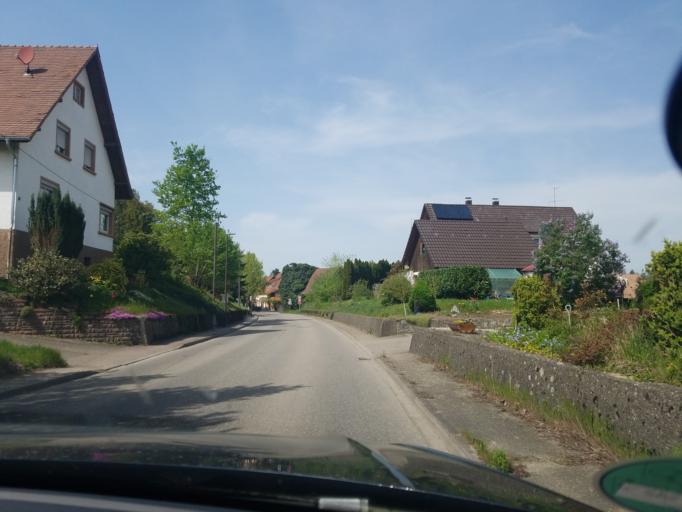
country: DE
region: Baden-Wuerttemberg
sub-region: Freiburg Region
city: Haslach
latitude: 48.5773
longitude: 8.0501
